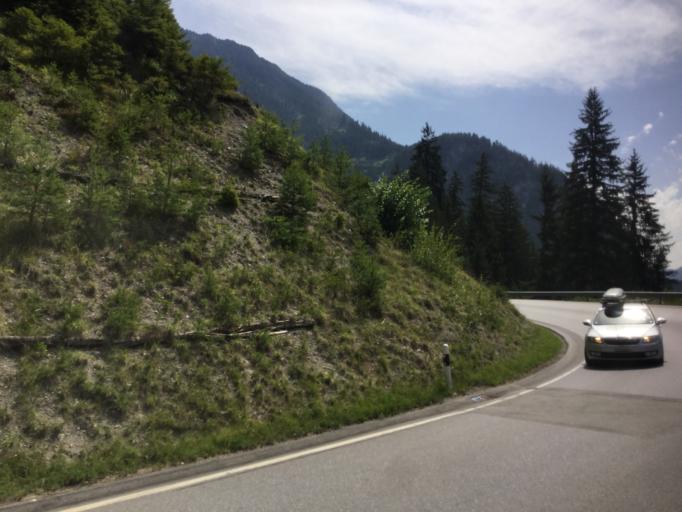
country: CH
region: Grisons
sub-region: Albula District
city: Tiefencastel
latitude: 46.6488
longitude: 9.5799
